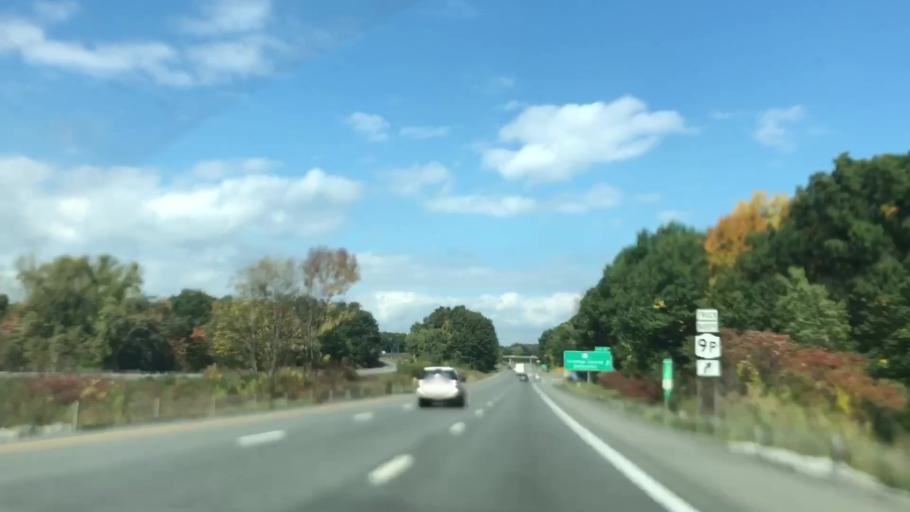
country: US
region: New York
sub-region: Saratoga County
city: Saratoga Springs
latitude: 43.0905
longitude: -73.7500
